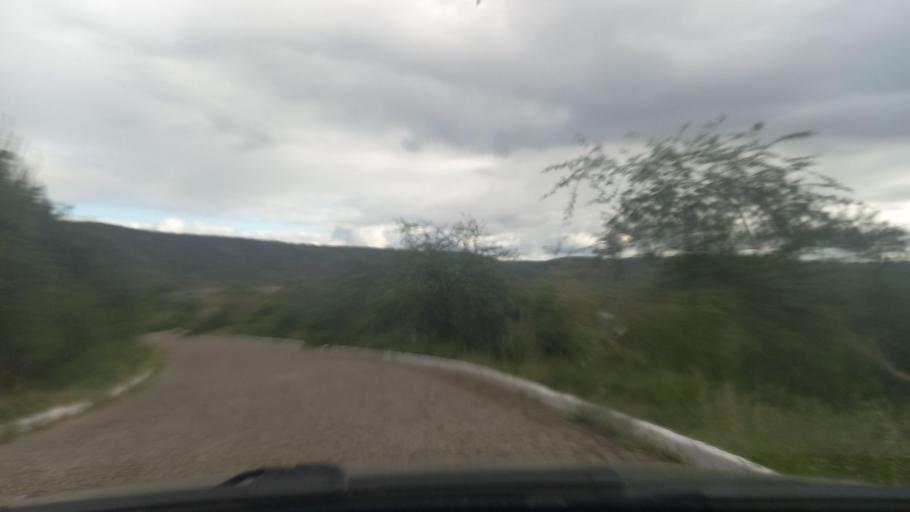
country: BR
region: Sergipe
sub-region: Caninde De Sao Francisco
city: Caninde de Sao Francisco
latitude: -9.6225
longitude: -37.8046
